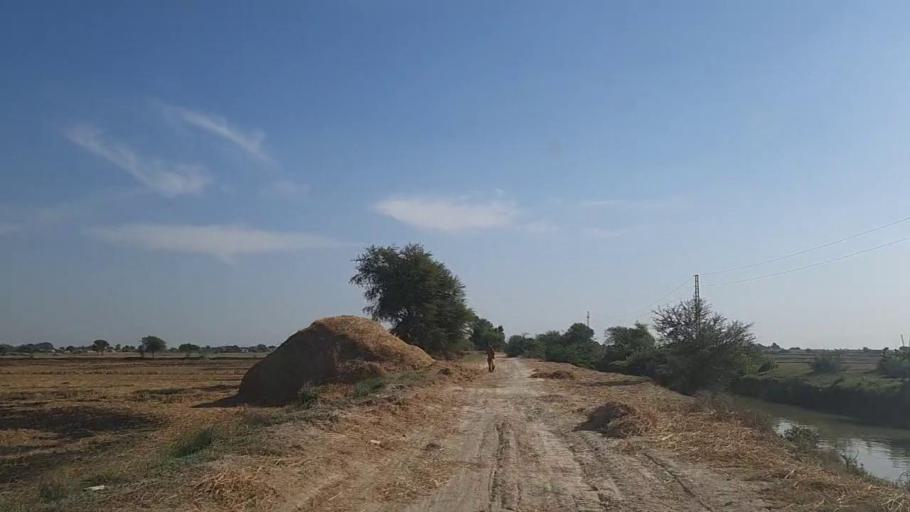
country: PK
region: Sindh
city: Bulri
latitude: 24.8655
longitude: 68.2837
